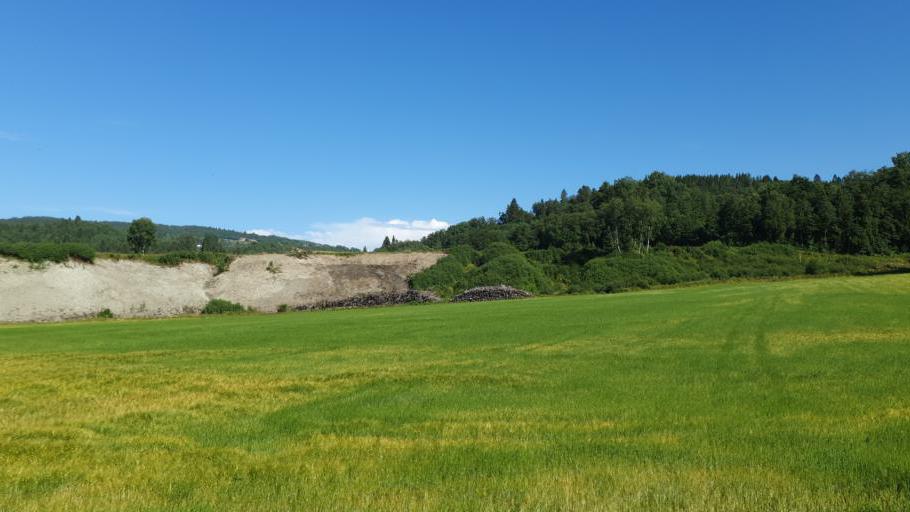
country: NO
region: Sor-Trondelag
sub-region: Orkdal
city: Orkanger
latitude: 63.1968
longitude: 9.7869
